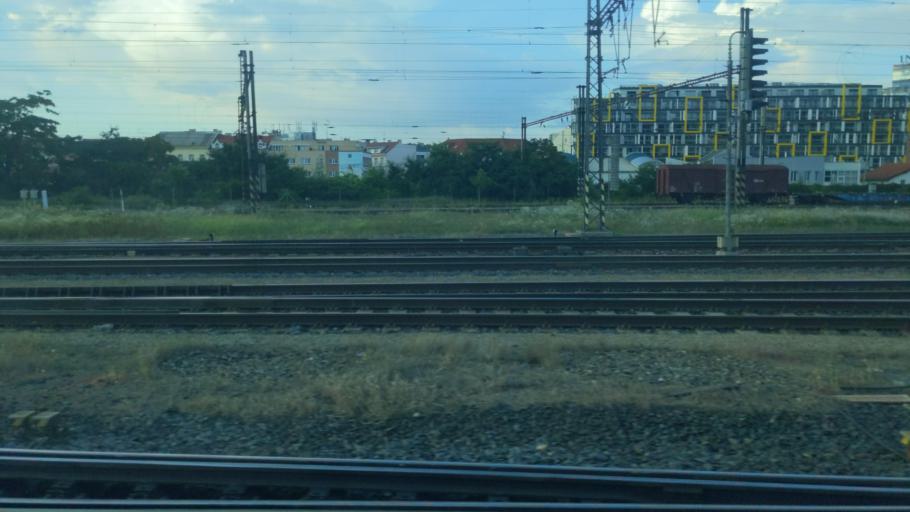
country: CZ
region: Praha
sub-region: Praha 8
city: Liben
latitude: 50.1022
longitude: 14.4872
